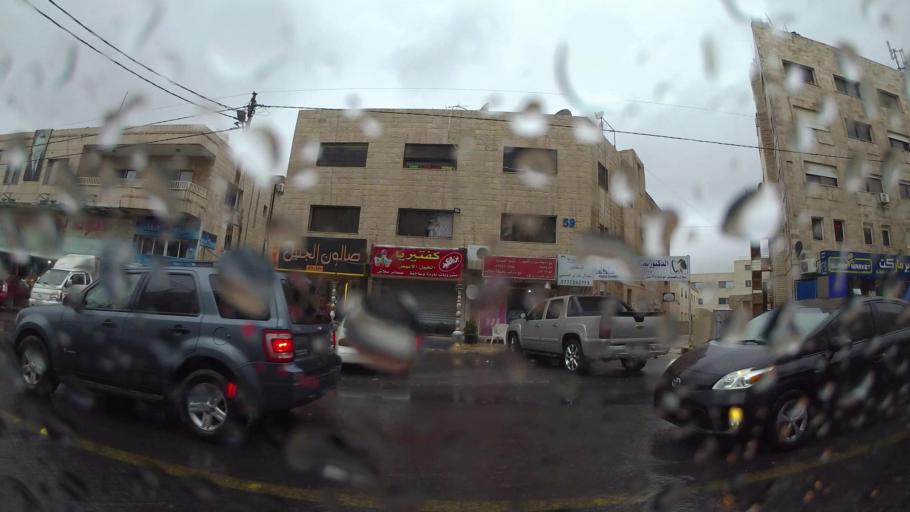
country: JO
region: Amman
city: Al Jubayhah
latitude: 32.0233
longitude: 35.8747
